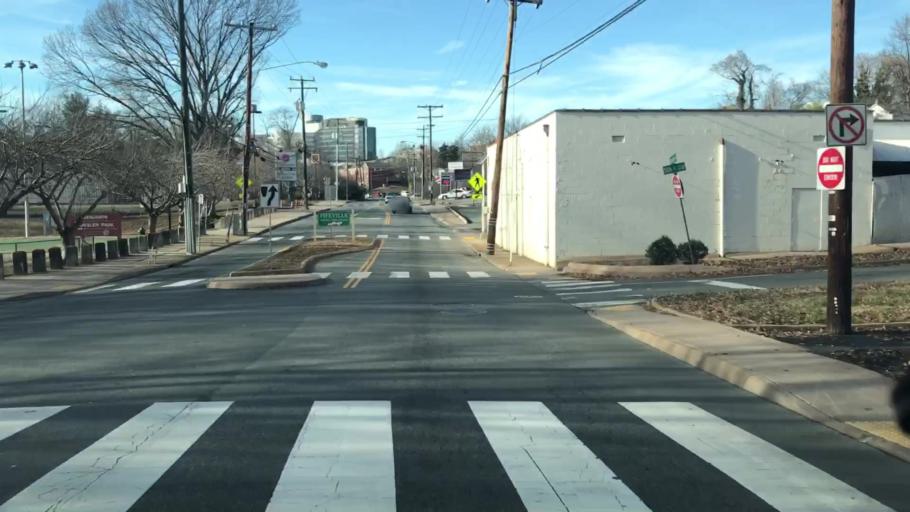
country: US
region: Virginia
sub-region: City of Charlottesville
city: Charlottesville
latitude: 38.0268
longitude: -78.4902
